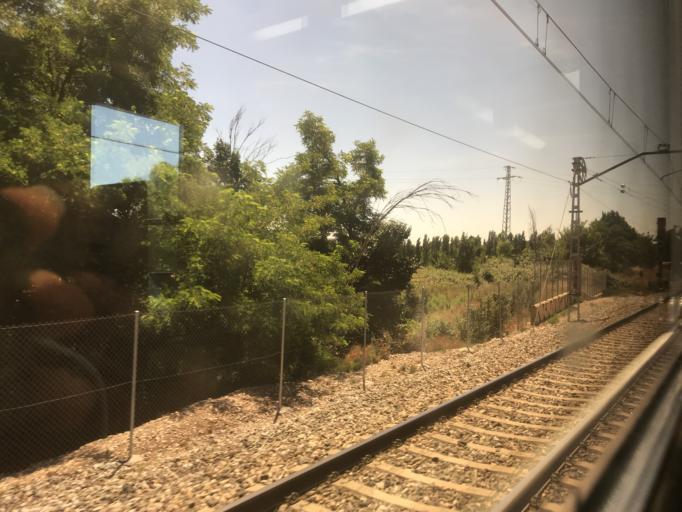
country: ES
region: Madrid
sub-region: Provincia de Madrid
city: Aranjuez
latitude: 40.0429
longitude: -3.6212
